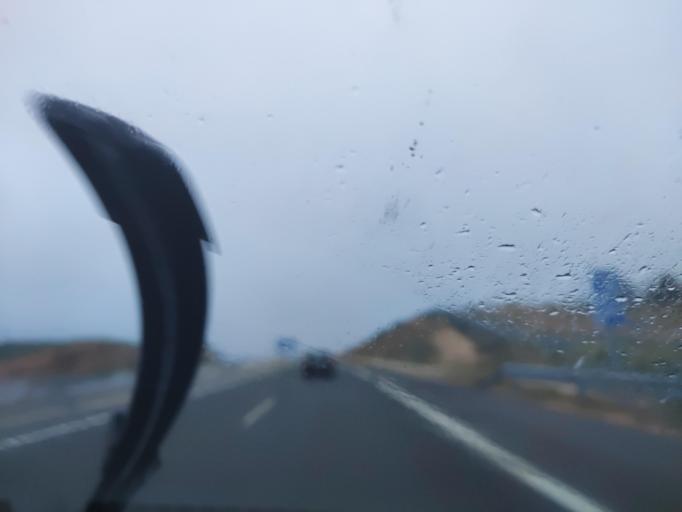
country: ES
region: Castille-La Mancha
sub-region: Province of Toledo
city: Bargas
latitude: 39.9085
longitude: -4.0618
